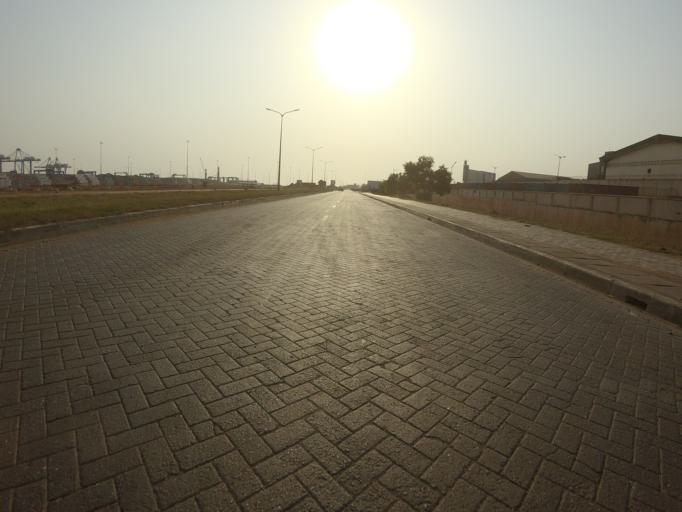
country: GH
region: Greater Accra
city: Tema
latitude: 5.6217
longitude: -0.0117
